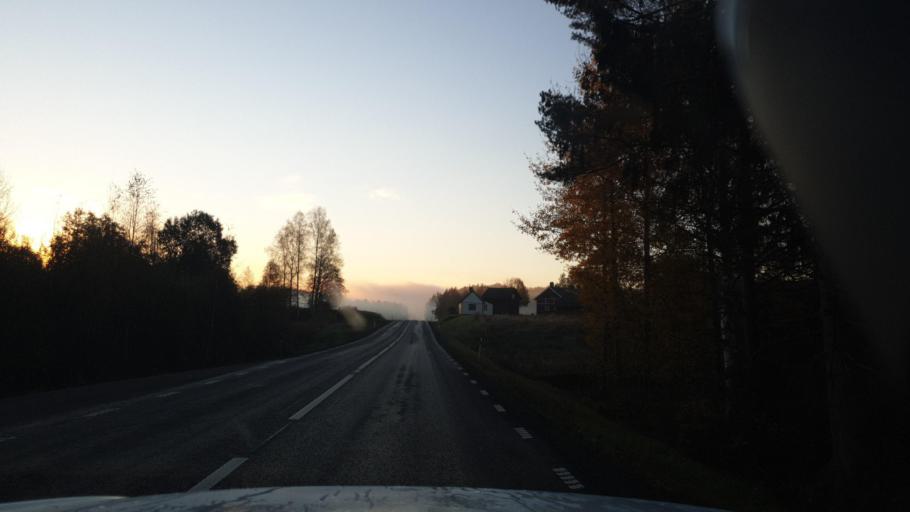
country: SE
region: Vaermland
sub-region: Eda Kommun
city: Charlottenberg
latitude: 59.8267
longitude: 12.3188
